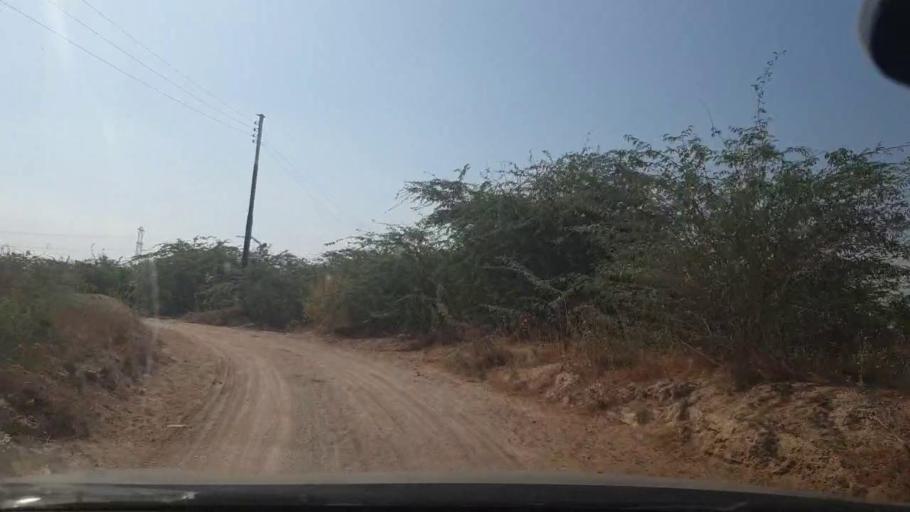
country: PK
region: Sindh
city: Malir Cantonment
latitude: 25.1668
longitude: 67.2044
